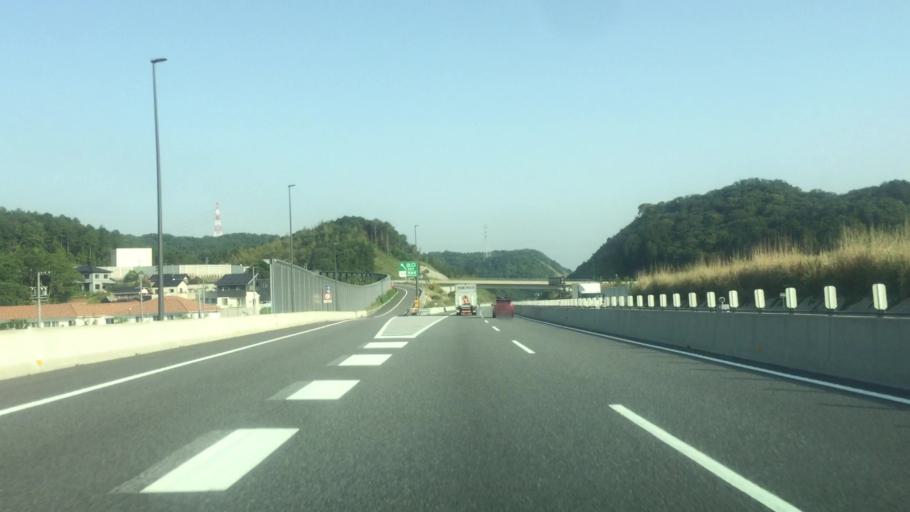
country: JP
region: Aichi
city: Gamagori
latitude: 34.9169
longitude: 137.2800
